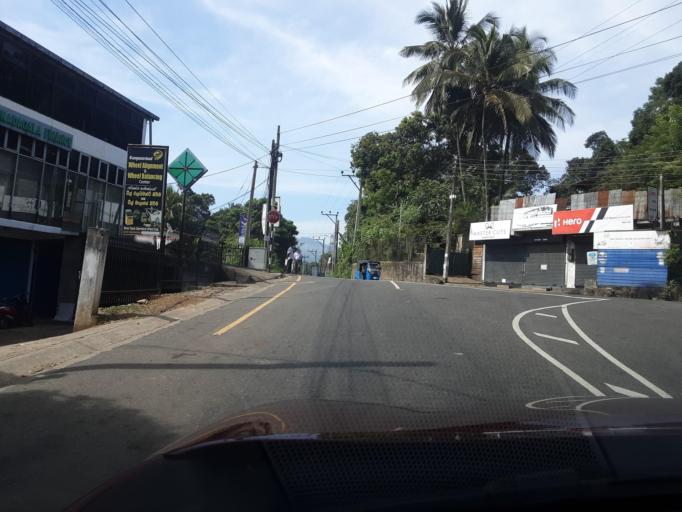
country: LK
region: Uva
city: Badulla
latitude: 6.9850
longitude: 81.0641
